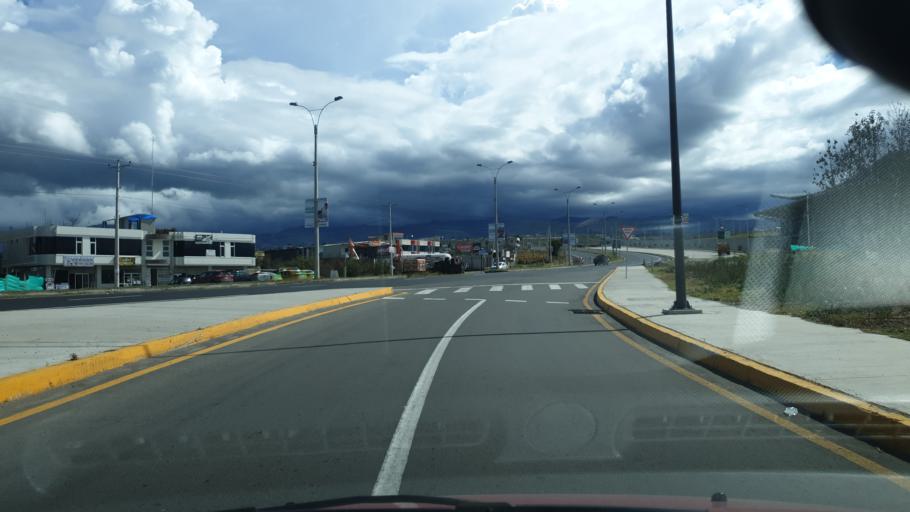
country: EC
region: Tungurahua
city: Ambato
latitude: -1.3004
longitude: -78.6323
